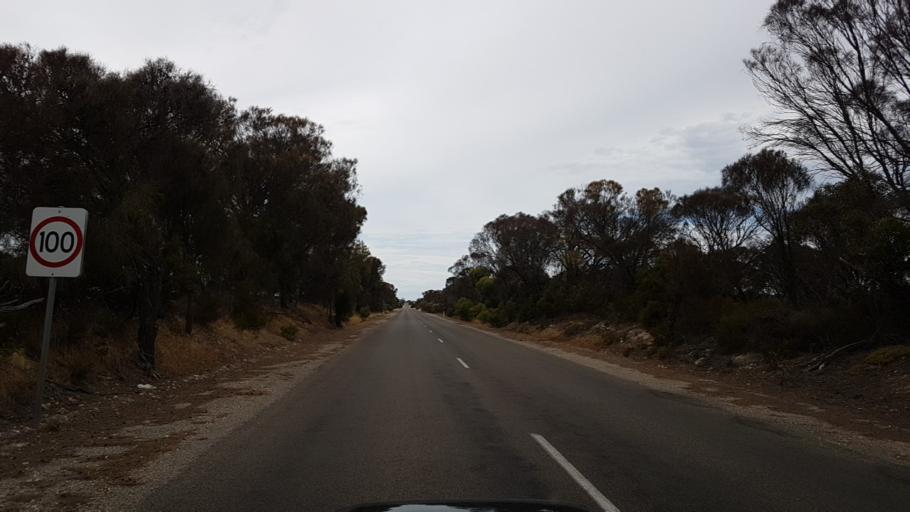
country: AU
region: South Australia
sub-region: Yorke Peninsula
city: Port Victoria
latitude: -34.9324
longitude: 137.0879
